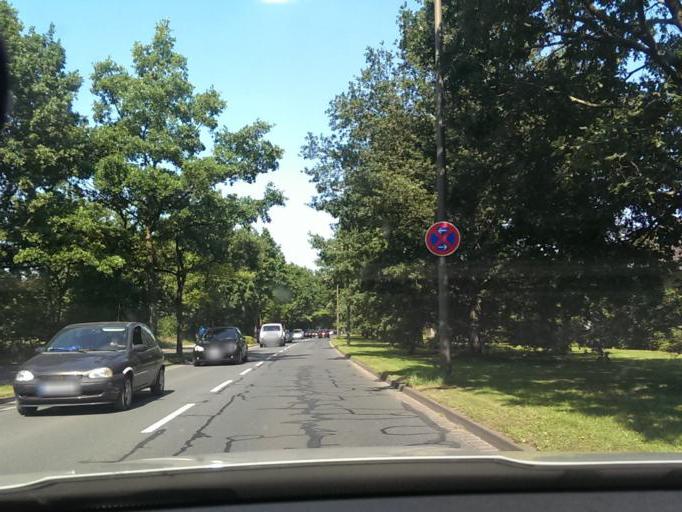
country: DE
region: Lower Saxony
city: Langenhagen
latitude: 52.4430
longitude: 9.7536
